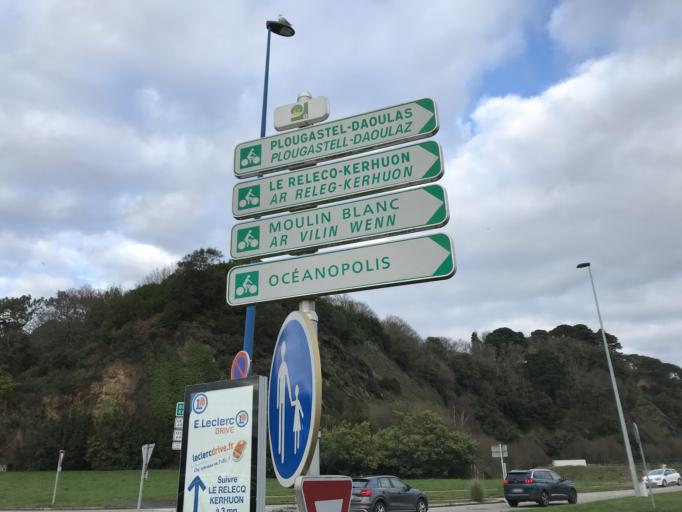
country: FR
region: Brittany
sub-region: Departement du Finistere
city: Brest
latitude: 48.3866
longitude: -4.4708
